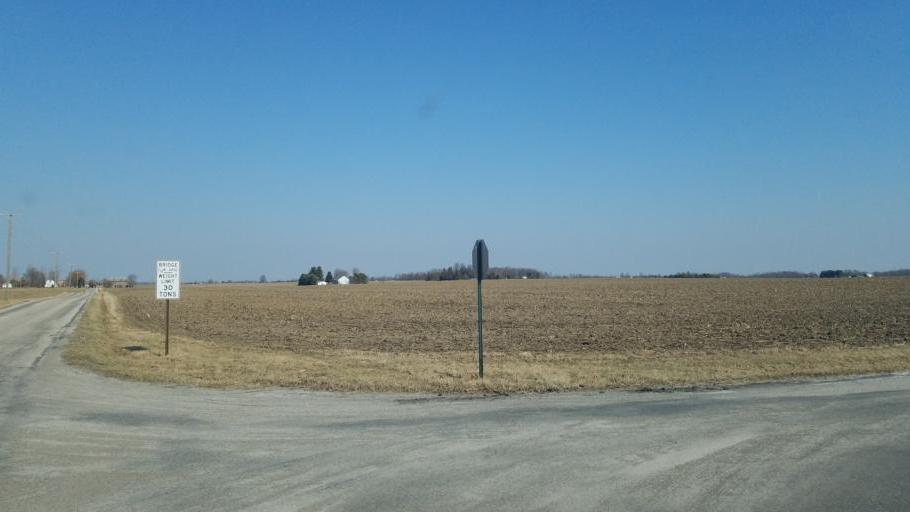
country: US
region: Ohio
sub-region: Crawford County
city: Crestline
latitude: 40.8295
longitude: -82.6957
